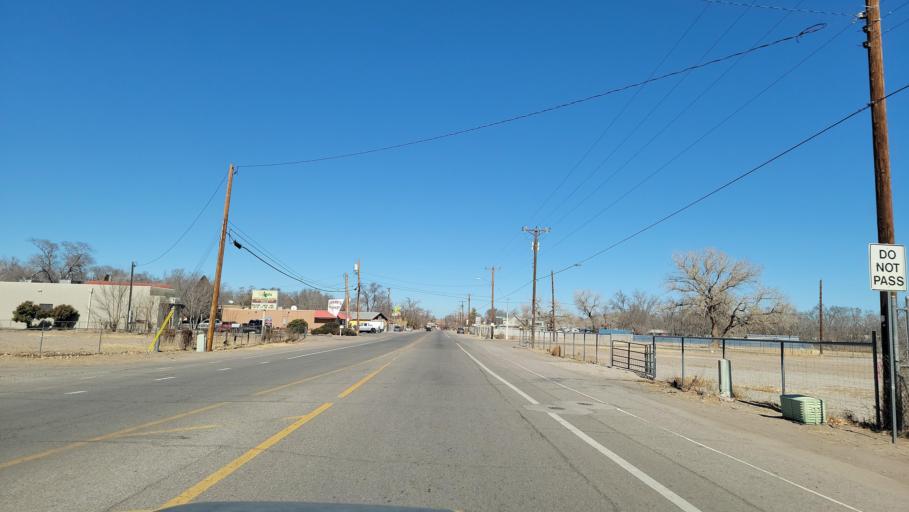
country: US
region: New Mexico
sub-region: Bernalillo County
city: South Valley
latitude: 34.9520
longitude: -106.6945
